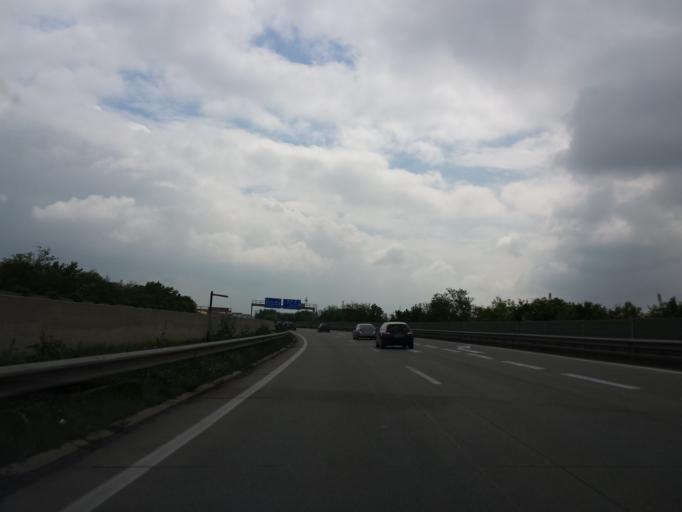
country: AT
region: Lower Austria
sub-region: Politischer Bezirk Wien-Umgebung
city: Schwechat
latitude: 48.1524
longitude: 16.4814
